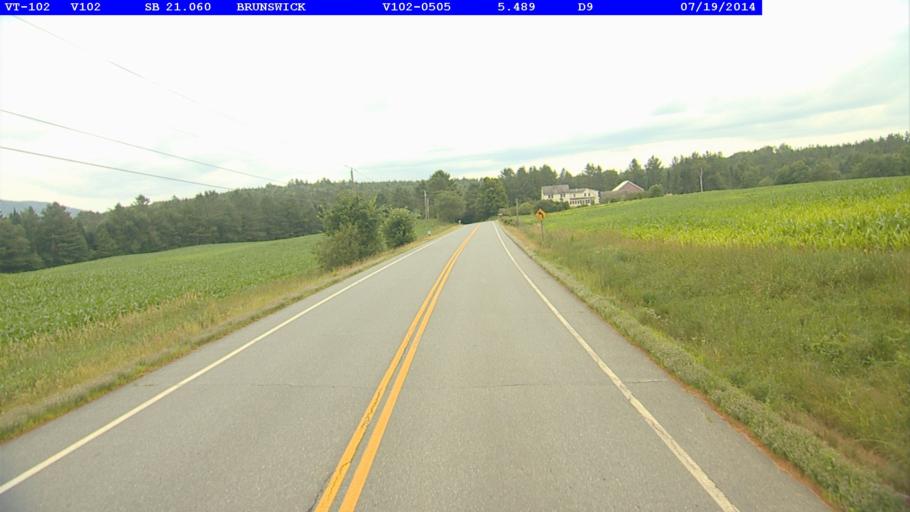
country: US
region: New Hampshire
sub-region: Coos County
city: Stratford
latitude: 44.7269
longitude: -71.6344
